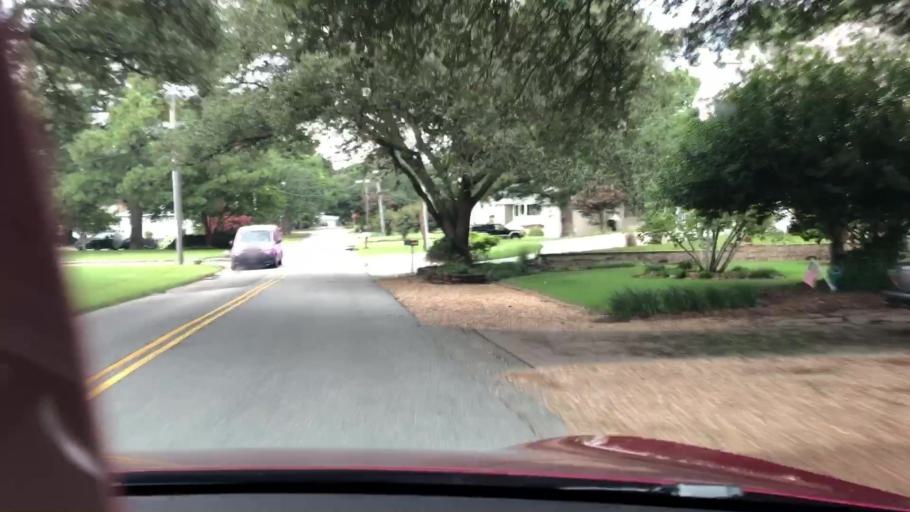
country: US
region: Virginia
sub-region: City of Virginia Beach
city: Virginia Beach
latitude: 36.9075
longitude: -76.0722
